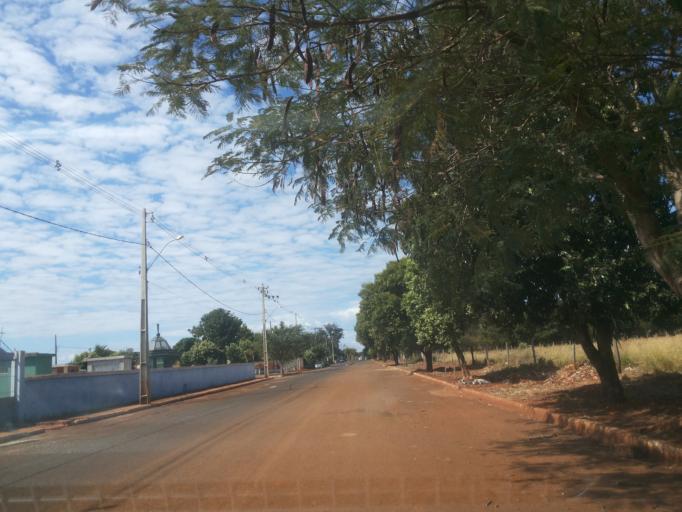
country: BR
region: Minas Gerais
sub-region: Centralina
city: Centralina
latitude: -18.5796
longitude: -49.2105
